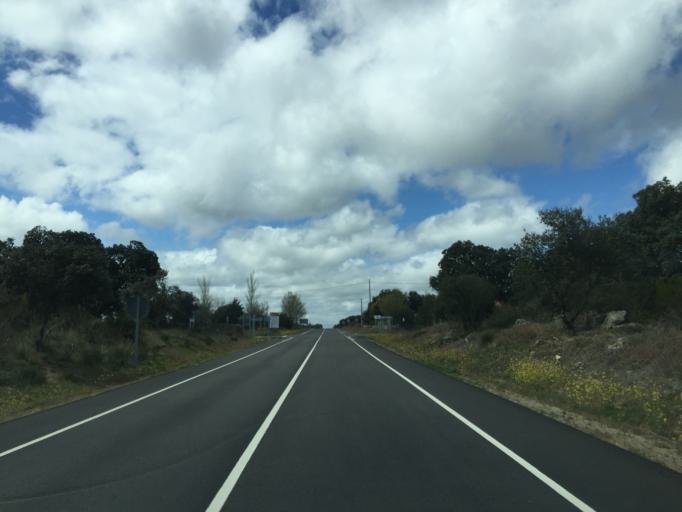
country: ES
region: Castille and Leon
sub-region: Provincia de Zamora
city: Torregamones
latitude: 41.4798
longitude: -6.1748
